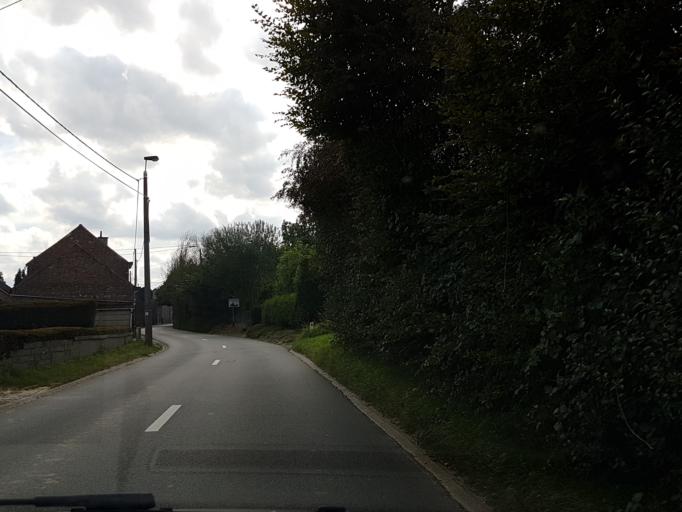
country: BE
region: Flanders
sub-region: Provincie Vlaams-Brabant
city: Oud-Heverlee
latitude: 50.8492
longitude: 4.6486
